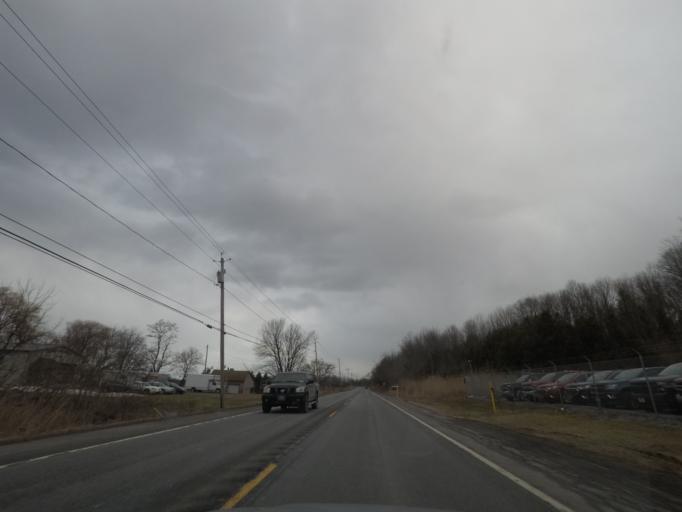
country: US
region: New York
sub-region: Madison County
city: Chittenango
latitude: 43.0543
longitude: -75.8549
